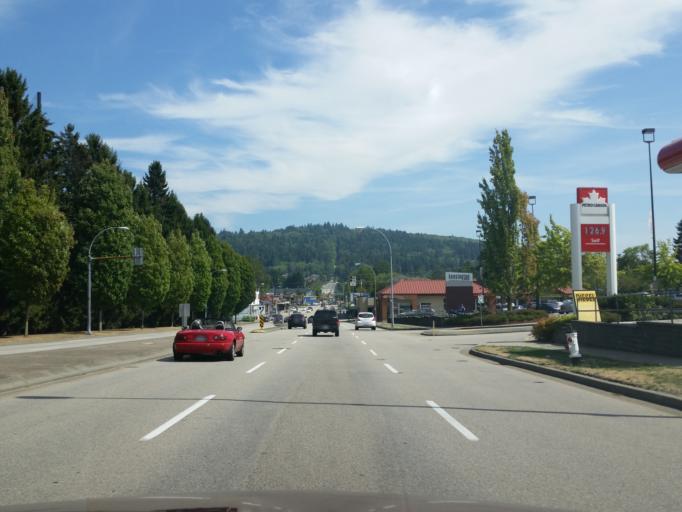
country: CA
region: British Columbia
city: Burnaby
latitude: 49.2803
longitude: -122.9686
